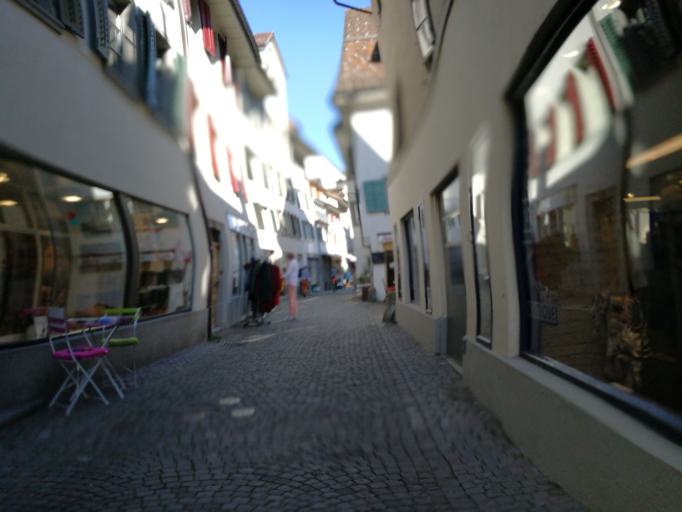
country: CH
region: Saint Gallen
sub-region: Wahlkreis See-Gaster
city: Rapperswil
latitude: 47.2274
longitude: 8.8176
